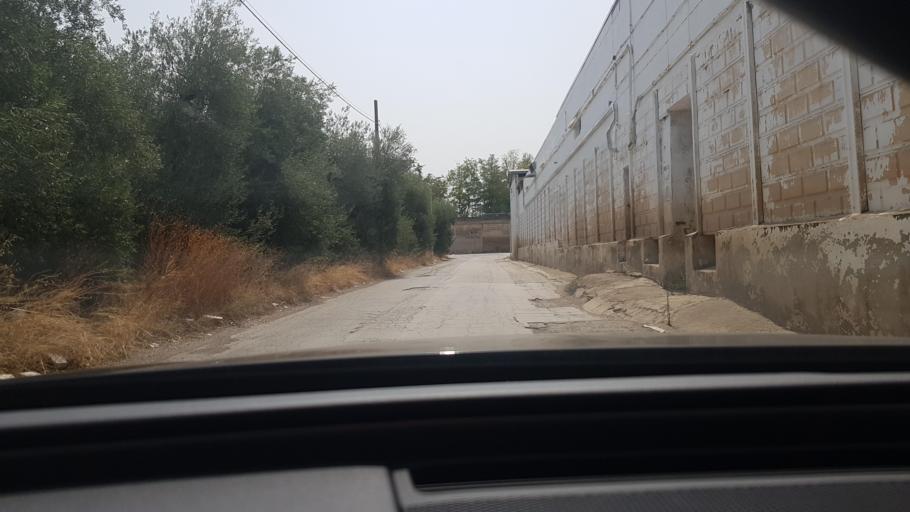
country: IT
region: Apulia
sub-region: Provincia di Barletta - Andria - Trani
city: Andria
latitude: 41.2157
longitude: 16.2611
